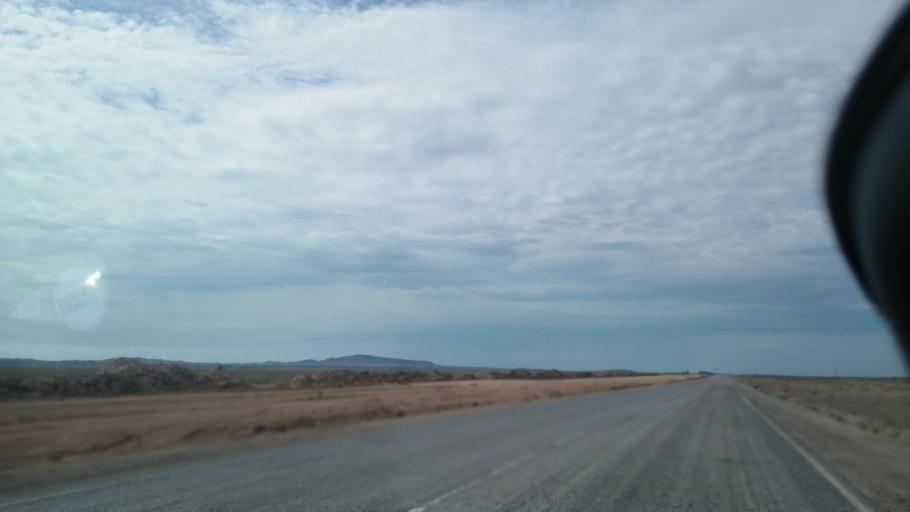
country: KZ
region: Qaraghandy
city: Balqash
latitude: 46.6974
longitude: 74.4432
